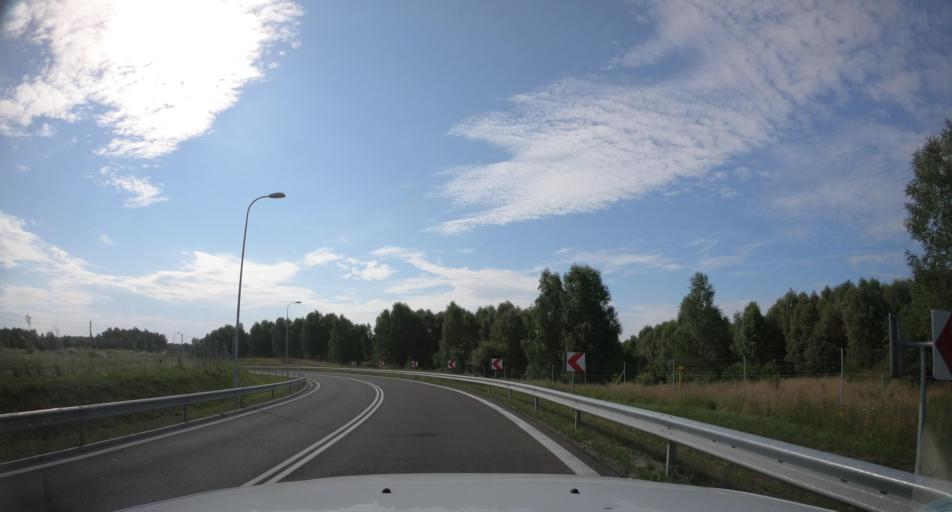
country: PL
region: West Pomeranian Voivodeship
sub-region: Powiat walecki
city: Walcz
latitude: 53.2932
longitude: 16.4547
